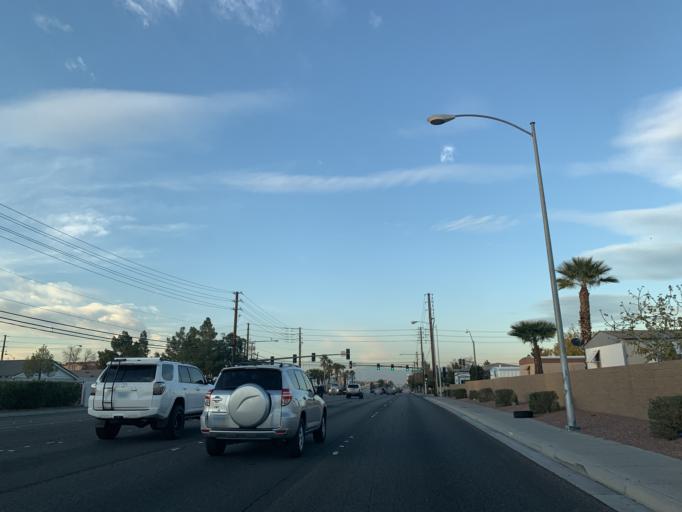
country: US
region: Nevada
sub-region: Clark County
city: Spring Valley
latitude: 36.1063
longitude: -115.2249
